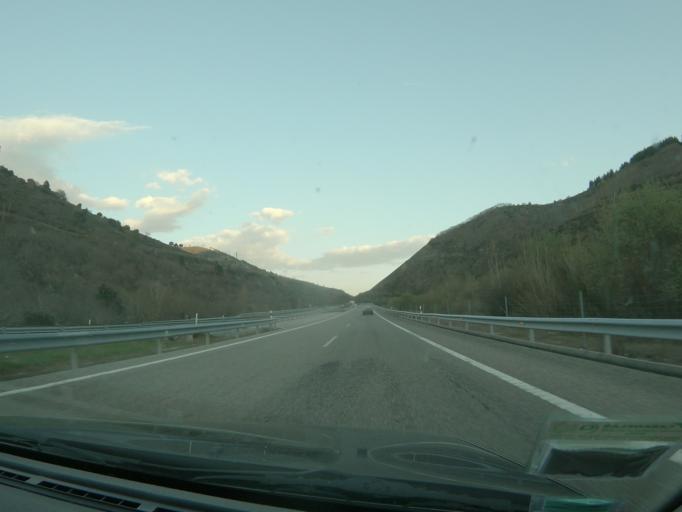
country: ES
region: Castille and Leon
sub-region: Provincia de Leon
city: Villafranca del Bierzo
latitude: 42.6240
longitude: -6.8424
